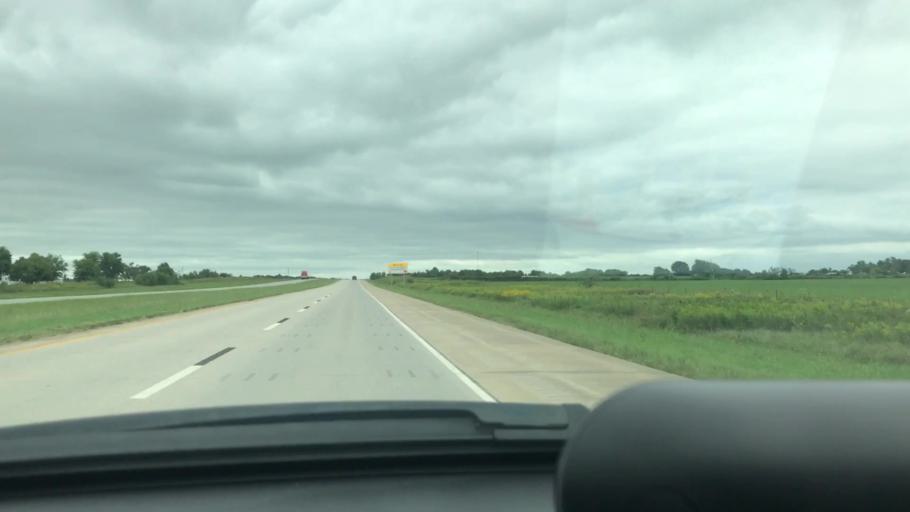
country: US
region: Oklahoma
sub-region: Mayes County
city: Chouteau
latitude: 36.0838
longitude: -95.3640
